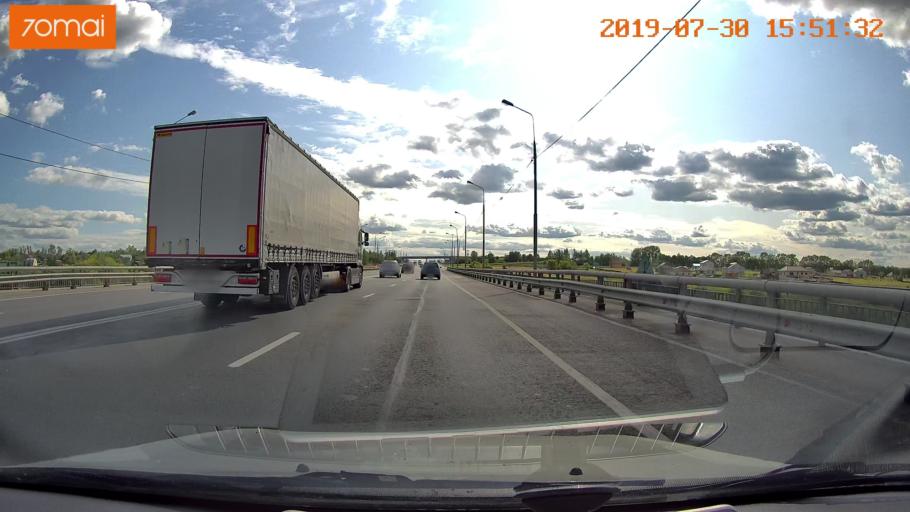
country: RU
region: Moskovskaya
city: Voskresensk
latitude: 55.3255
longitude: 38.6400
